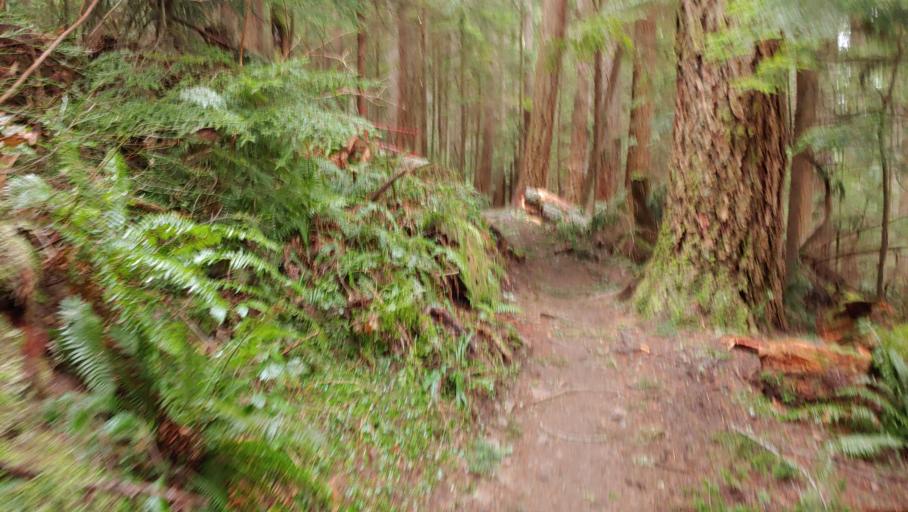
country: US
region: Washington
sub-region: King County
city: Hobart
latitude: 47.4713
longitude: -121.9198
